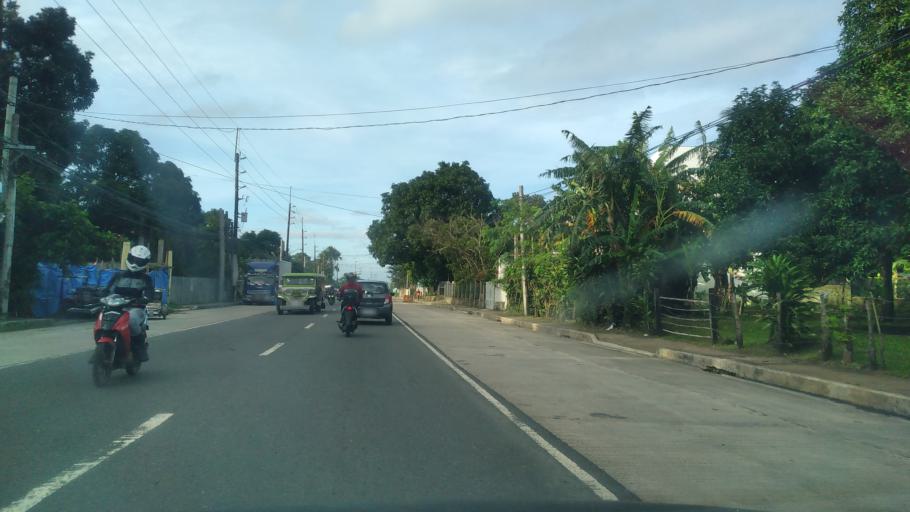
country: PH
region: Calabarzon
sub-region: Province of Quezon
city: Calumpang
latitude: 13.9709
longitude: 121.5518
